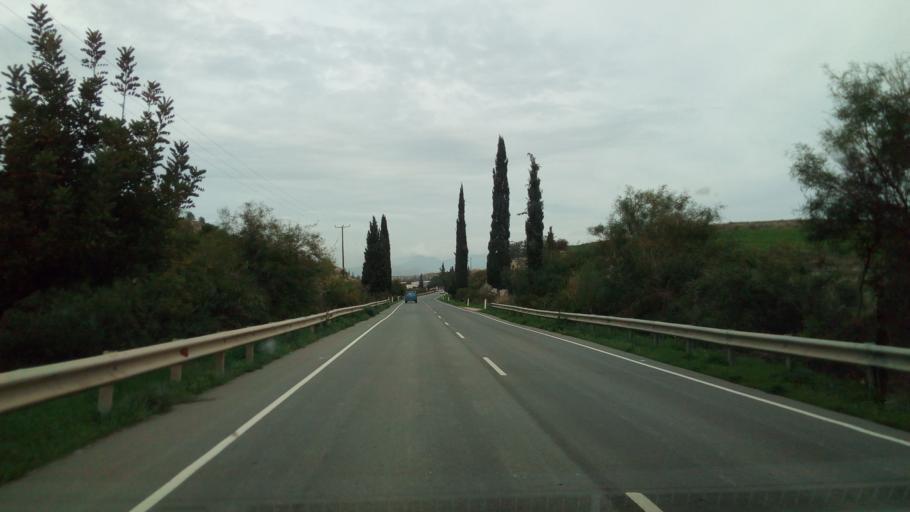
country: CY
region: Lefkosia
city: Astromeritis
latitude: 35.0918
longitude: 32.9644
